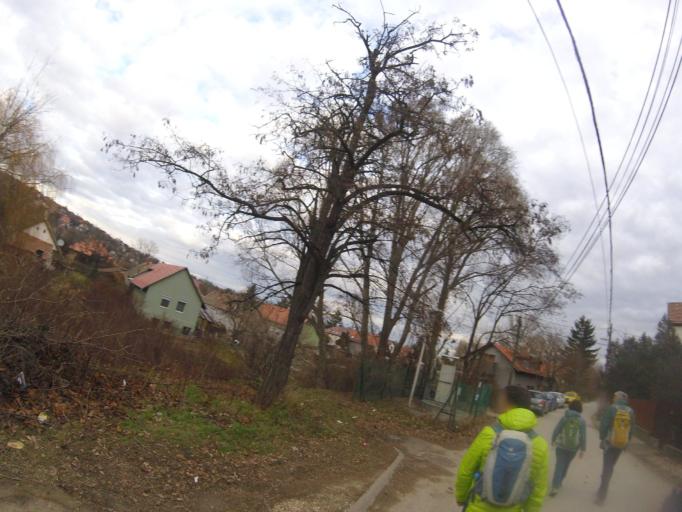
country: HU
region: Pest
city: Nagykovacsi
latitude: 47.6467
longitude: 19.0131
